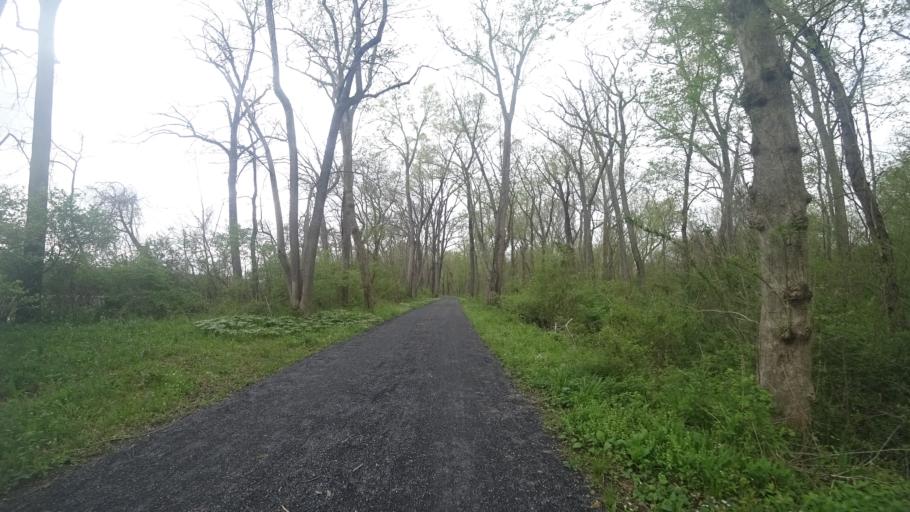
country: US
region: Virginia
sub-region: Loudoun County
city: University Center
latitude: 39.0738
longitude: -77.4167
